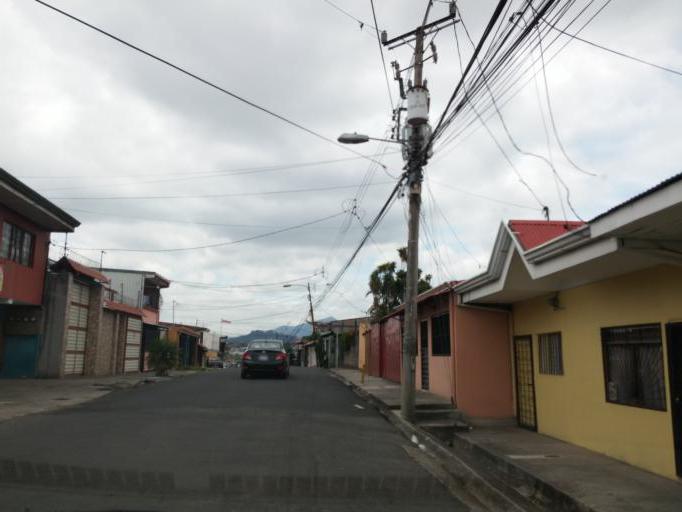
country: CR
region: San Jose
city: Alajuelita
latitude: 9.9059
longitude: -84.0814
